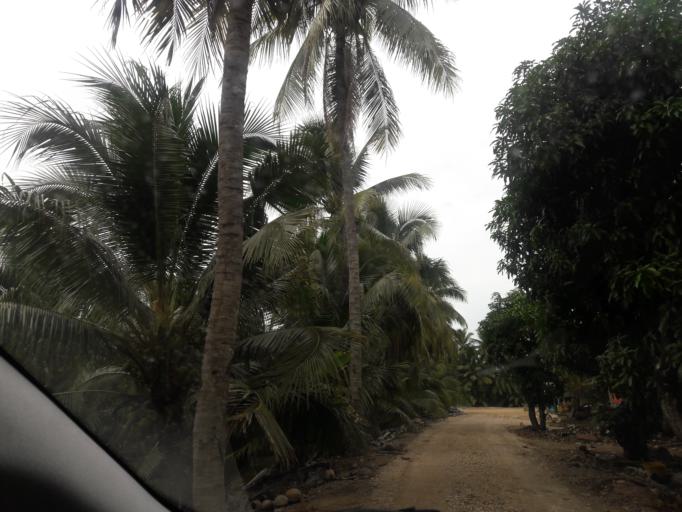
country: TH
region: Ratchaburi
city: Damnoen Saduak
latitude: 13.5373
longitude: 99.9327
